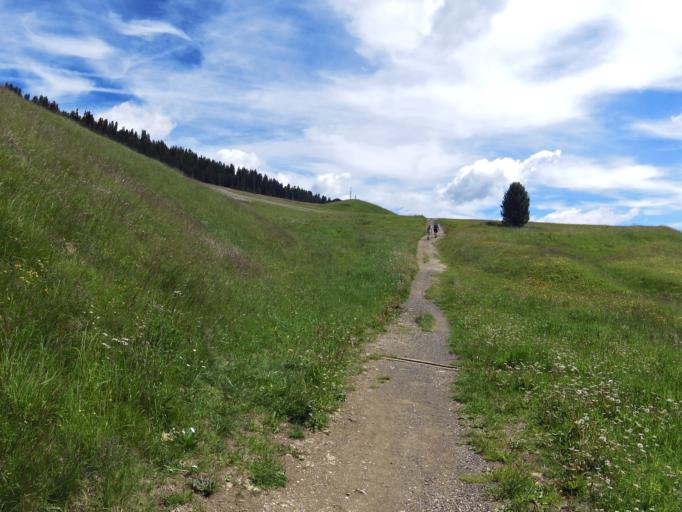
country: IT
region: Trentino-Alto Adige
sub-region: Bolzano
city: Ortisei
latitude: 46.5517
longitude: 11.6587
